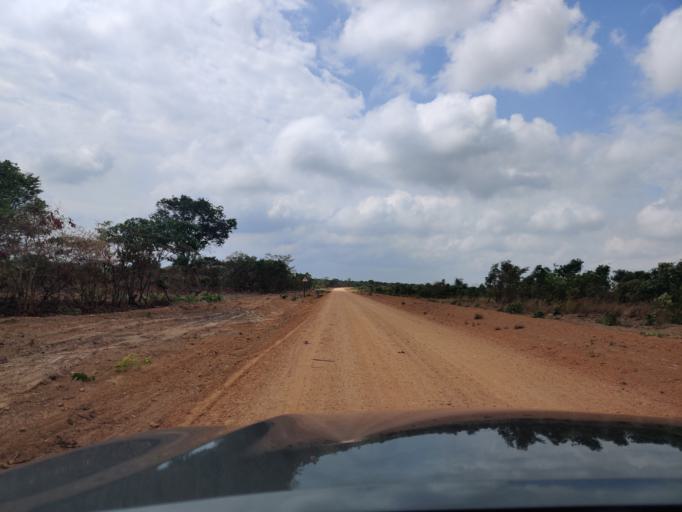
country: ZM
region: Central
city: Mkushi
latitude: -13.6567
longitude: 29.7519
